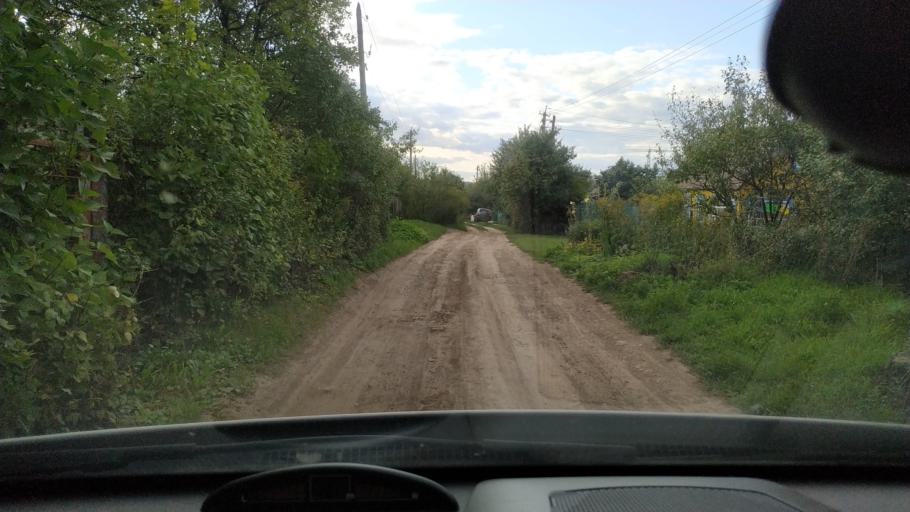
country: RU
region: Rjazan
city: Polyany
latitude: 54.5564
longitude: 39.8719
